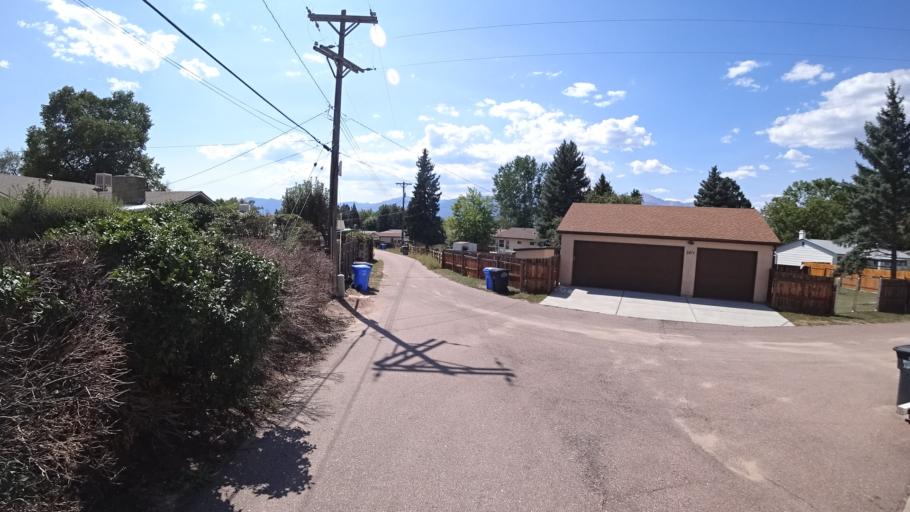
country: US
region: Colorado
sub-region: El Paso County
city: Colorado Springs
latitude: 38.8832
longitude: -104.8065
